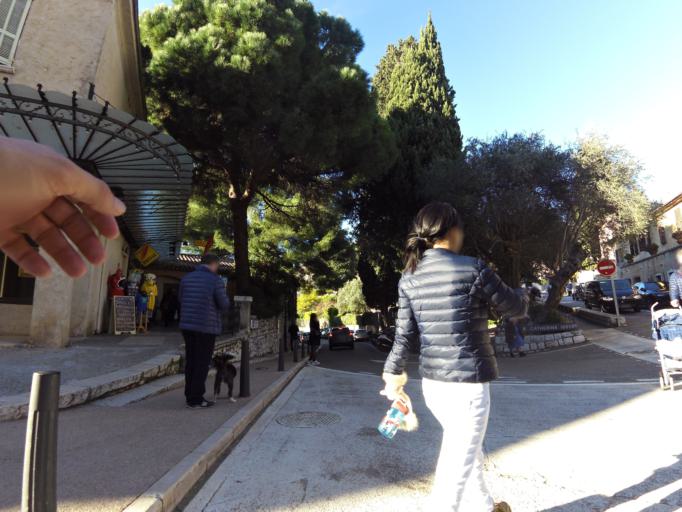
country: FR
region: Provence-Alpes-Cote d'Azur
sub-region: Departement des Alpes-Maritimes
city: Saint-Paul-de-Vence
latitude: 43.6985
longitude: 7.1219
